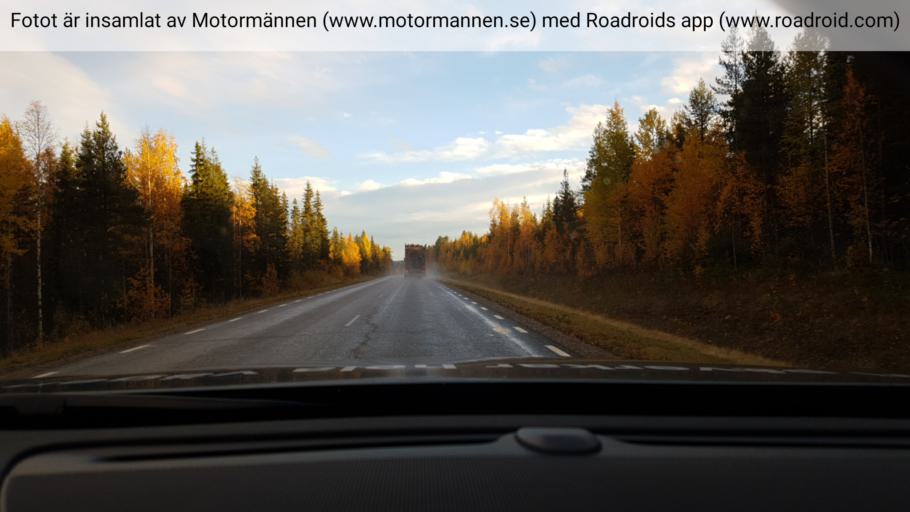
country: SE
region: Norrbotten
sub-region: Overkalix Kommun
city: OEverkalix
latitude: 66.6828
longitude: 22.6787
